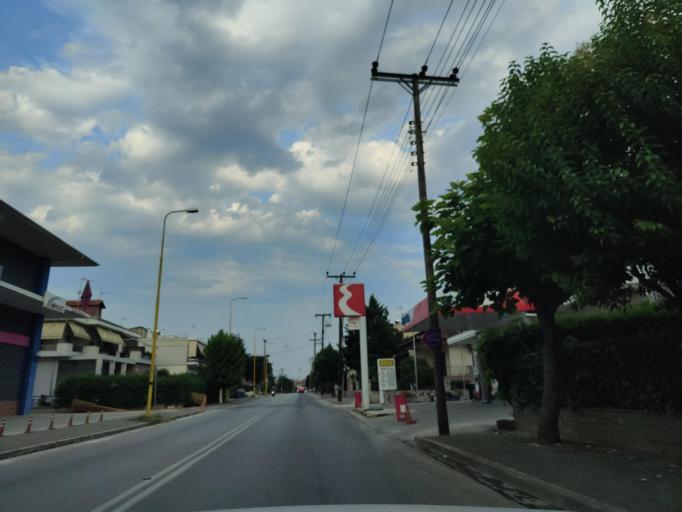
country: GR
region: East Macedonia and Thrace
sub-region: Nomos Dramas
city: Drama
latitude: 41.1531
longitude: 24.1262
